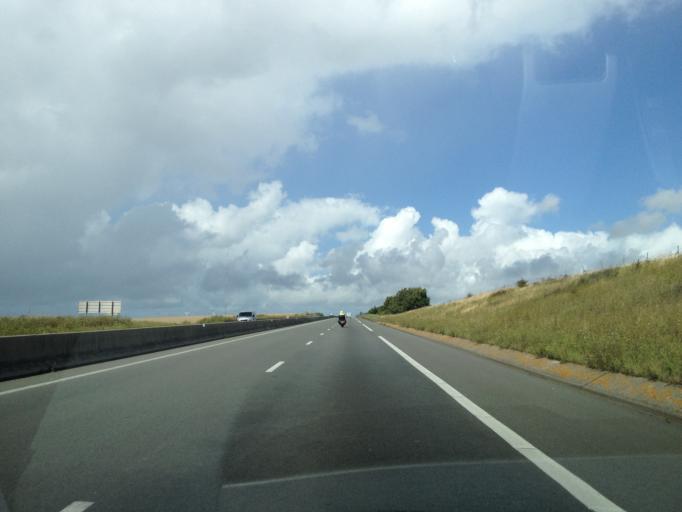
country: FR
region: Nord-Pas-de-Calais
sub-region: Departement du Pas-de-Calais
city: Etaples
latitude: 50.5536
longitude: 1.6707
